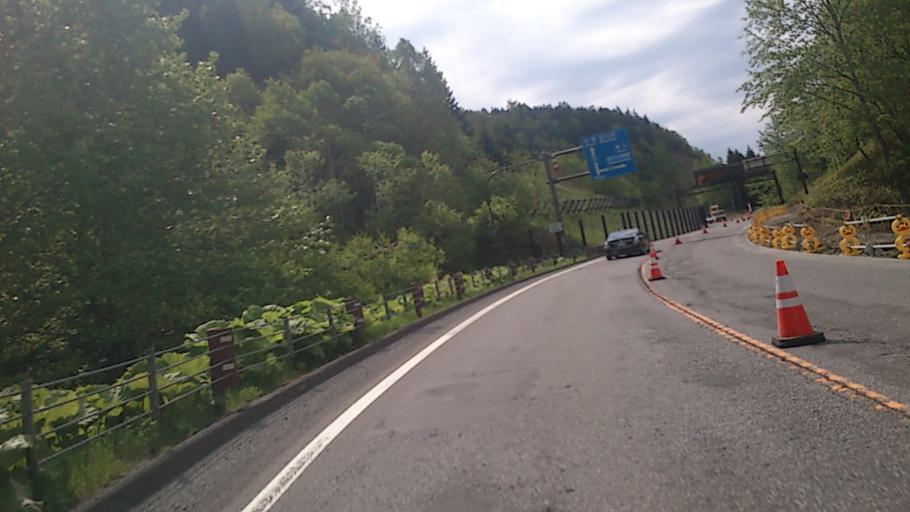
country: JP
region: Hokkaido
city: Kamikawa
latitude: 43.6828
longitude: 143.0346
